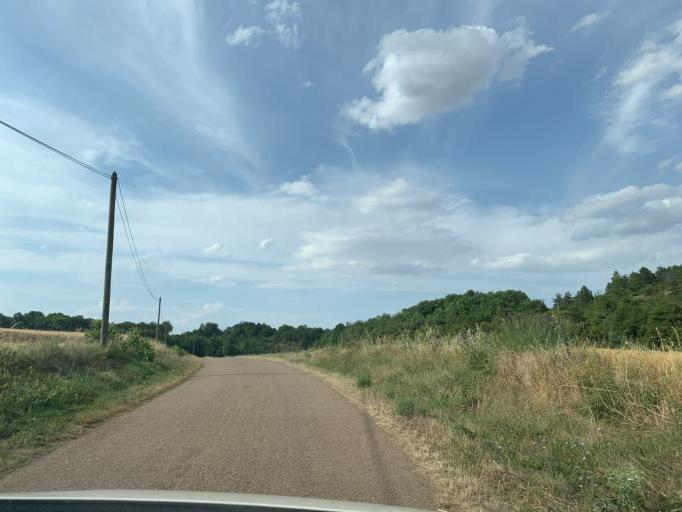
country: FR
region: Bourgogne
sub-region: Departement de l'Yonne
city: Fontenailles
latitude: 47.4837
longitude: 3.4202
